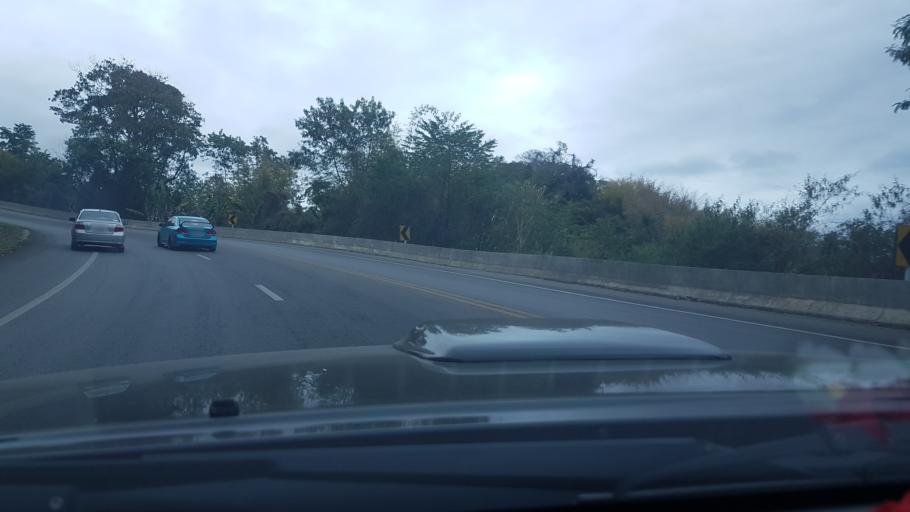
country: TH
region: Phetchabun
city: Khao Kho
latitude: 16.5495
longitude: 101.0338
